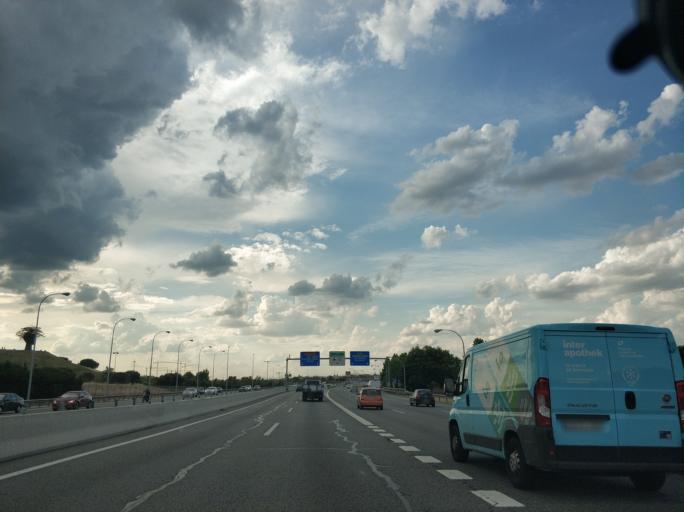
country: ES
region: Madrid
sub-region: Provincia de Madrid
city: Usera
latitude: 40.3764
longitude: -3.6836
